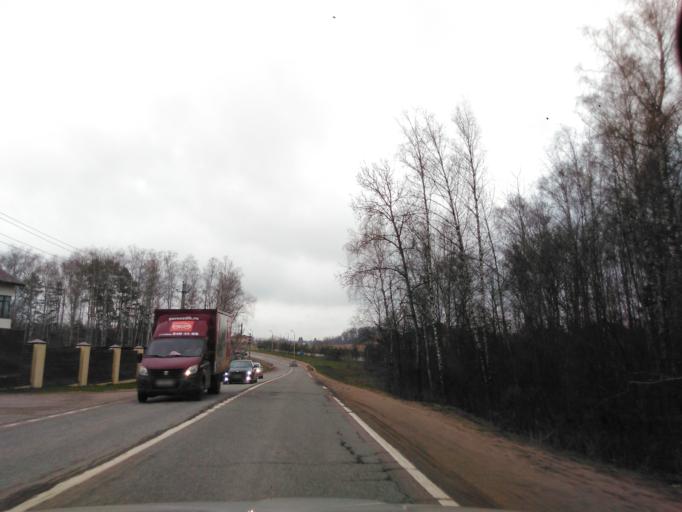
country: RU
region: Moskovskaya
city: Snegiri
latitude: 55.8433
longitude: 36.9890
